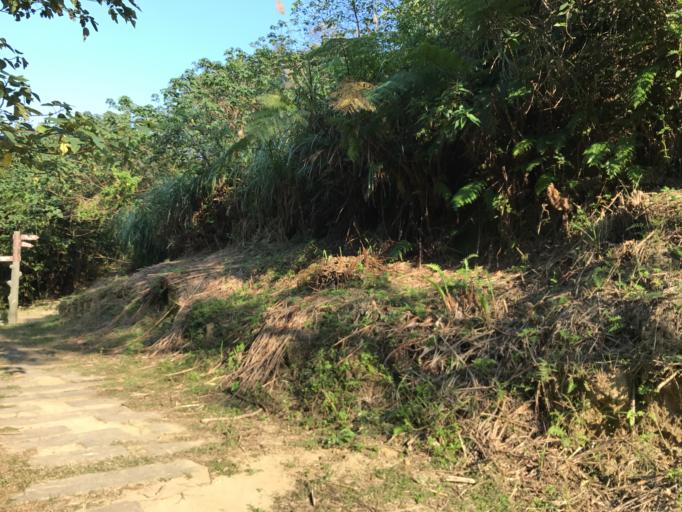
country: TW
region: Taiwan
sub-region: Hsinchu
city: Hsinchu
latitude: 24.7713
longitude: 120.9324
